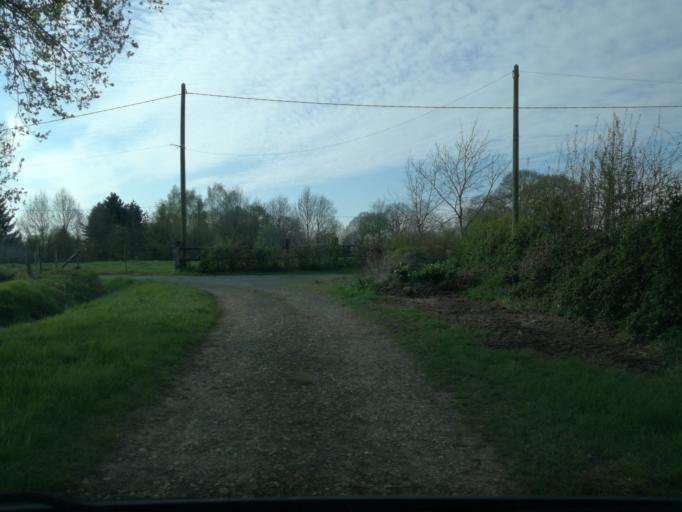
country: FR
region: Pays de la Loire
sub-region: Departement de la Sarthe
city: Brulon
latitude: 48.0535
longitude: -0.2482
